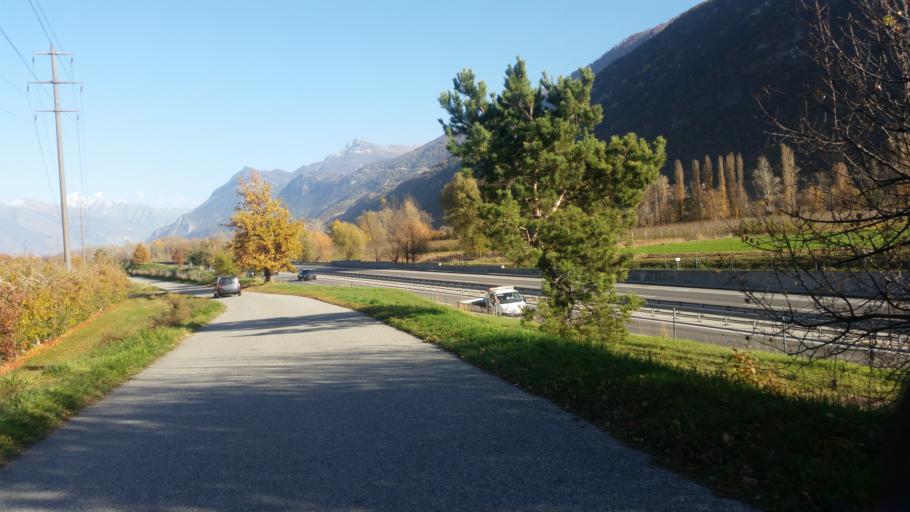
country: CH
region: Valais
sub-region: Sion District
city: Saint-Leonard
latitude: 46.2471
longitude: 7.4220
